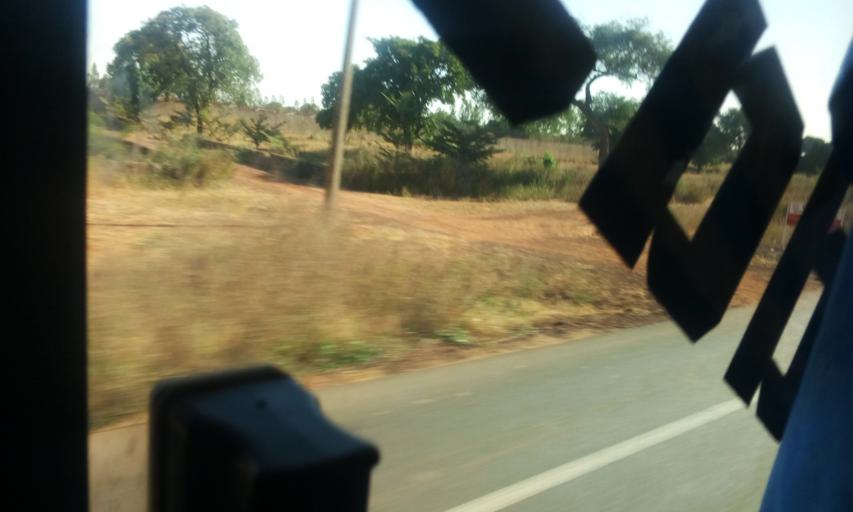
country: ML
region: Segou
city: Segou
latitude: 13.4065
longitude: -6.3313
